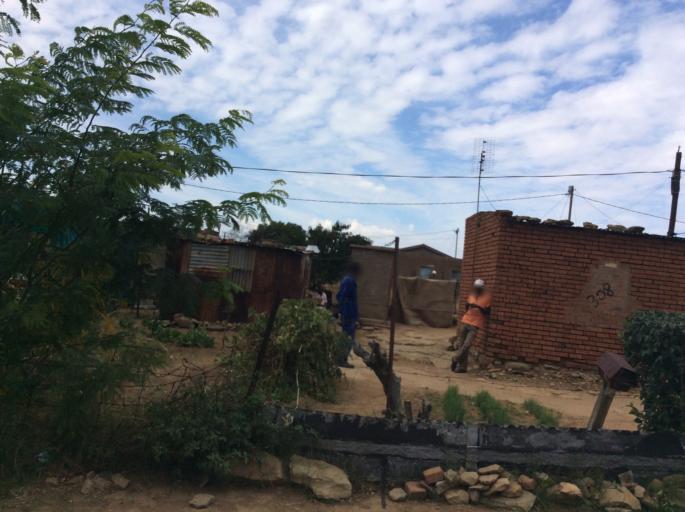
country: LS
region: Mafeteng
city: Mafeteng
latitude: -29.7219
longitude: 27.0307
